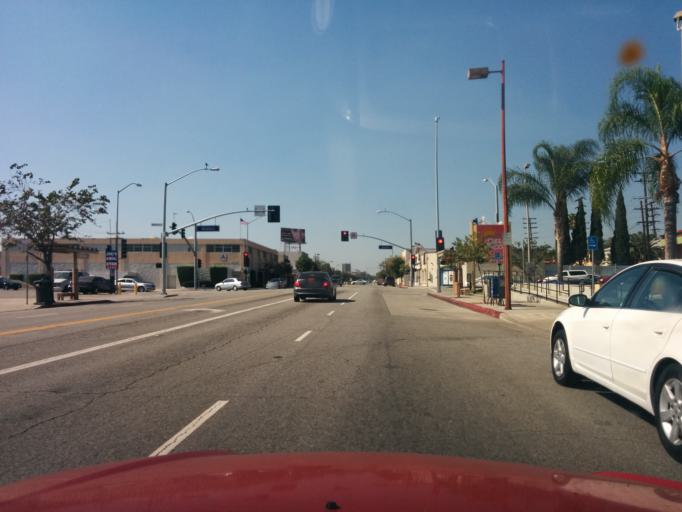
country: US
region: California
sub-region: Los Angeles County
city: Burbank
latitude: 34.1685
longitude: -118.2916
